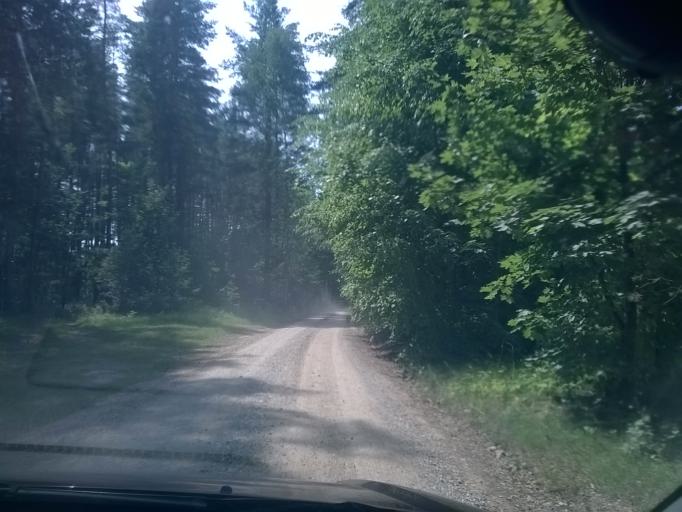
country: EE
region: Tartu
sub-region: Puhja vald
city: Puhja
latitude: 58.2516
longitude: 26.1741
